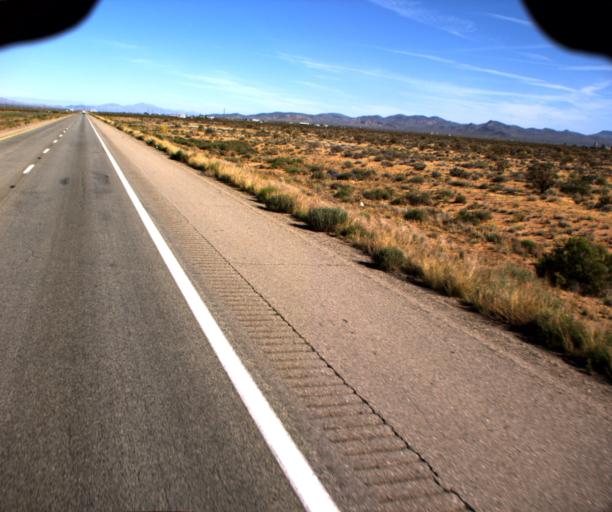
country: US
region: Arizona
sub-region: Mohave County
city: Dolan Springs
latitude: 35.5106
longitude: -114.3390
